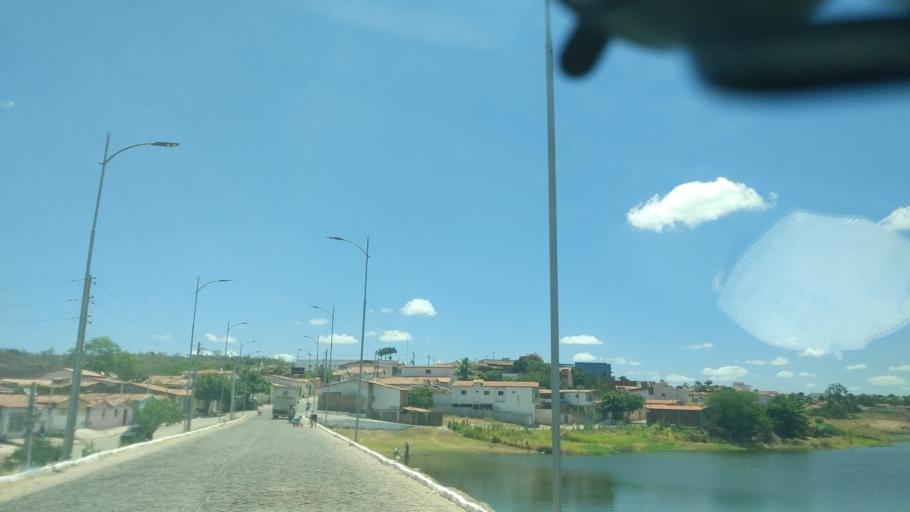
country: BR
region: Rio Grande do Norte
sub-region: Cerro Cora
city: Cerro Cora
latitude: -6.0415
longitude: -36.3464
